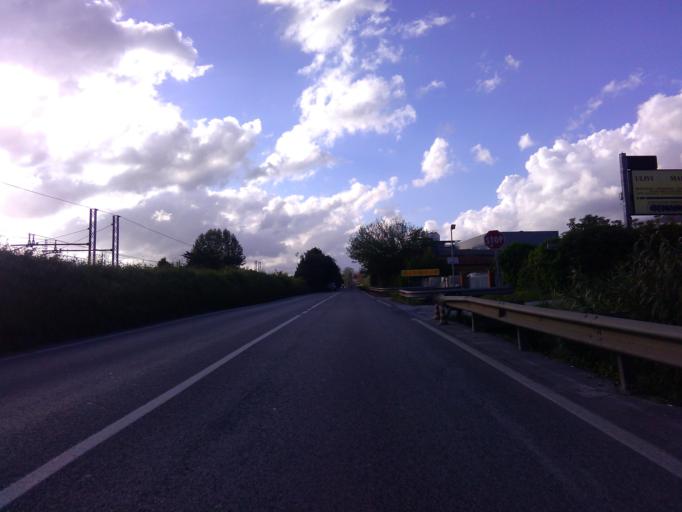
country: IT
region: Tuscany
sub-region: Provincia di Massa-Carrara
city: Capanne-Prato-Cinquale
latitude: 44.0027
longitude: 10.1654
